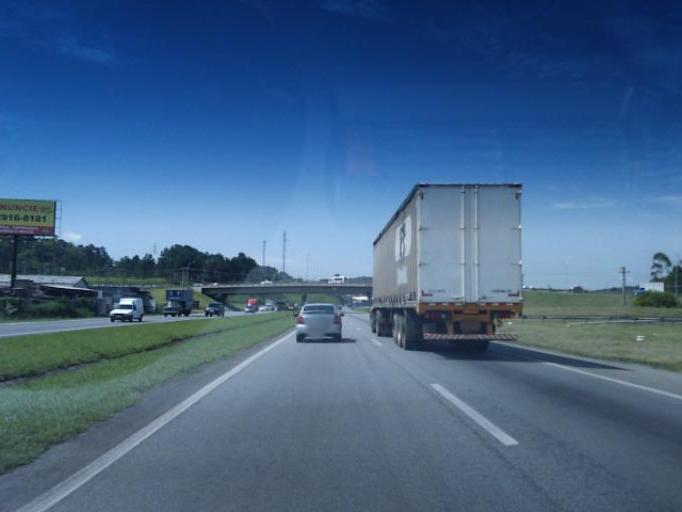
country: BR
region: Sao Paulo
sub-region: Embu
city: Embu
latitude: -23.6812
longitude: -46.8588
